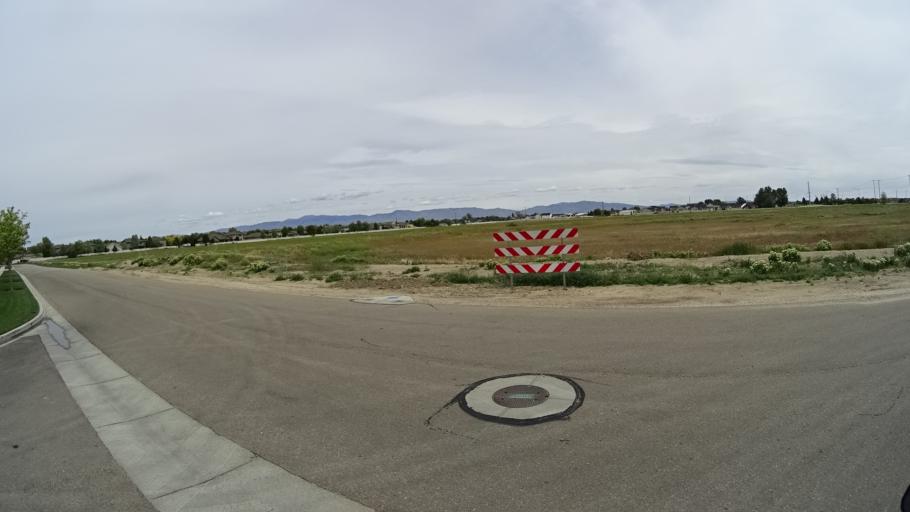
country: US
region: Idaho
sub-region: Ada County
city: Meridian
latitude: 43.5626
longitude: -116.3598
